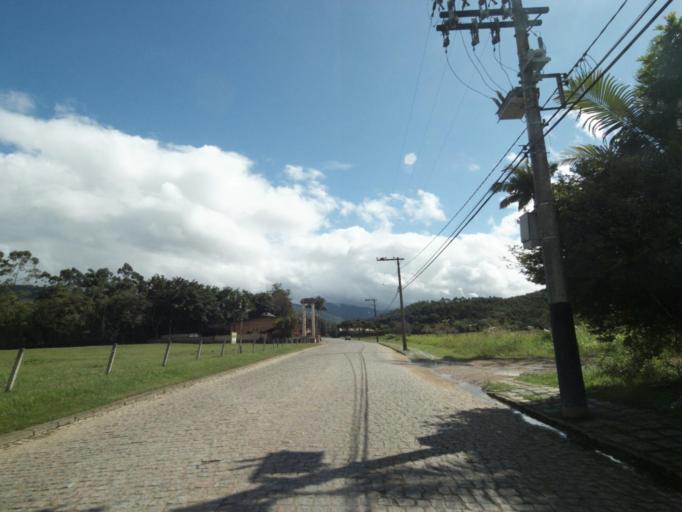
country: BR
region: Santa Catarina
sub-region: Pomerode
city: Pomerode
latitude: -26.7066
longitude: -49.1652
